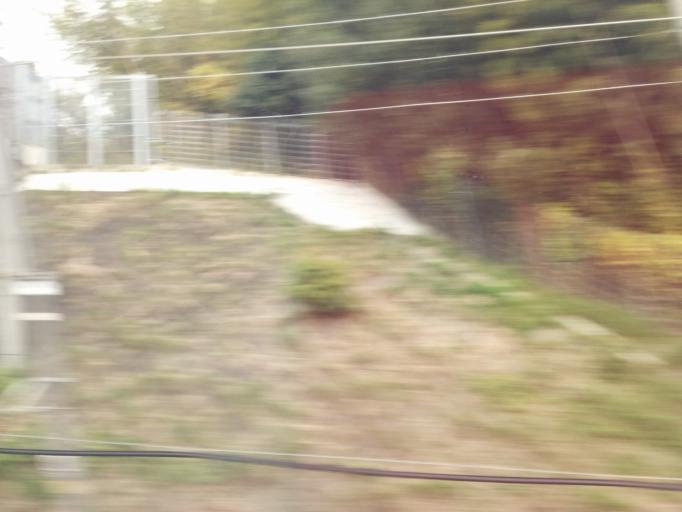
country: JP
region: Shizuoka
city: Numazu
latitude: 35.1405
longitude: 138.8131
